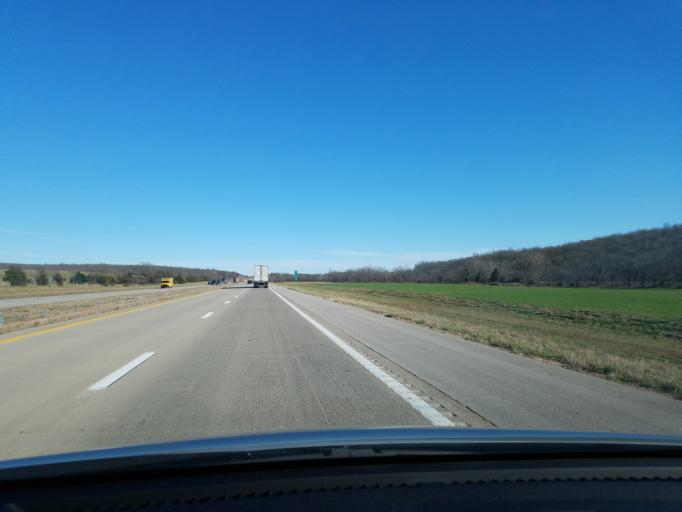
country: US
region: Missouri
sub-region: Laclede County
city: Lebanon
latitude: 37.7533
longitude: -92.5643
